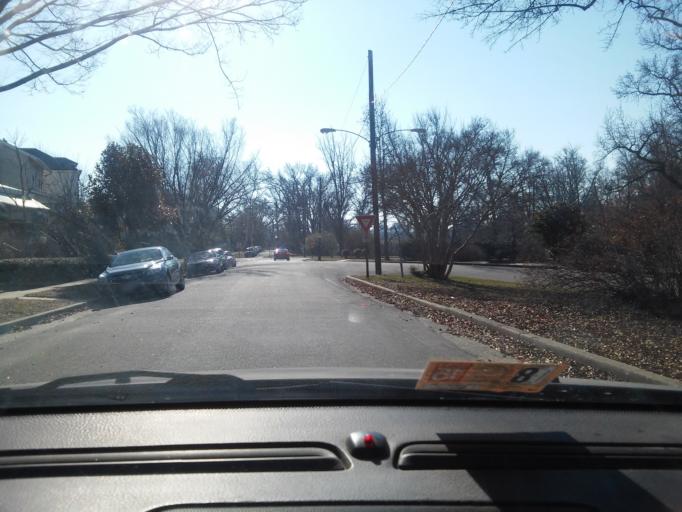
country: US
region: Virginia
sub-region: City of Richmond
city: Richmond
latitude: 37.5662
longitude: -77.4387
